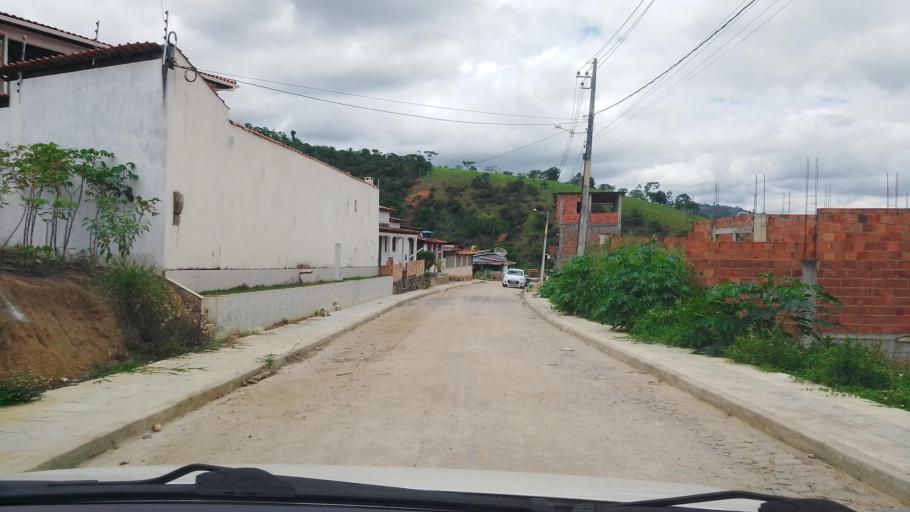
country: BR
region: Bahia
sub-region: Mutuipe
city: Mutuipe
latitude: -13.2567
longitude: -39.5659
